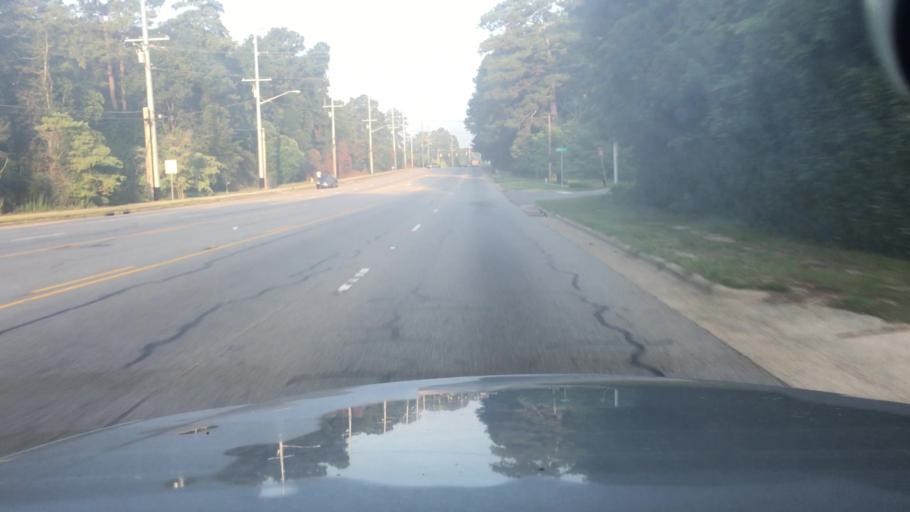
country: US
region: North Carolina
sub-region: Cumberland County
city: Fayetteville
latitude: 35.1048
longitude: -78.8823
